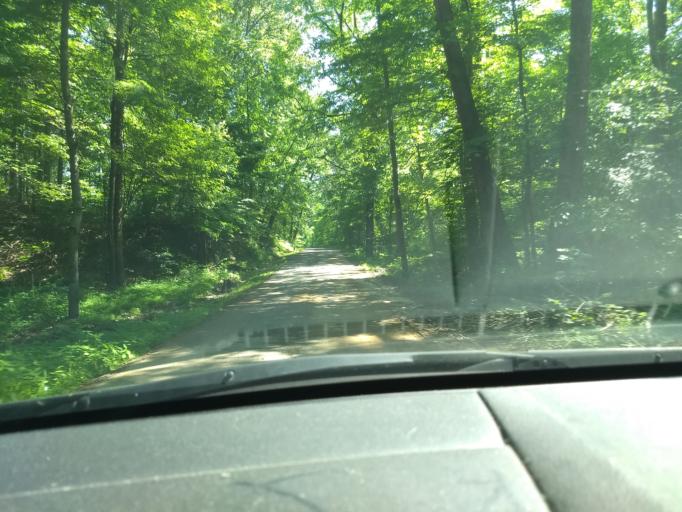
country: US
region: Indiana
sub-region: Floyd County
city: New Albany
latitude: 38.2761
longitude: -85.8667
